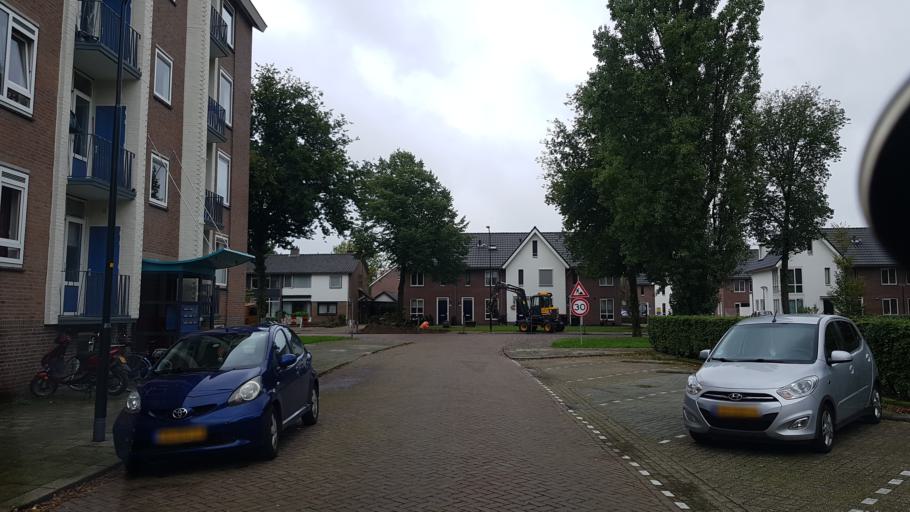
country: NL
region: Gelderland
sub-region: Gemeente Apeldoorn
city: Apeldoorn
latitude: 52.1933
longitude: 5.9551
